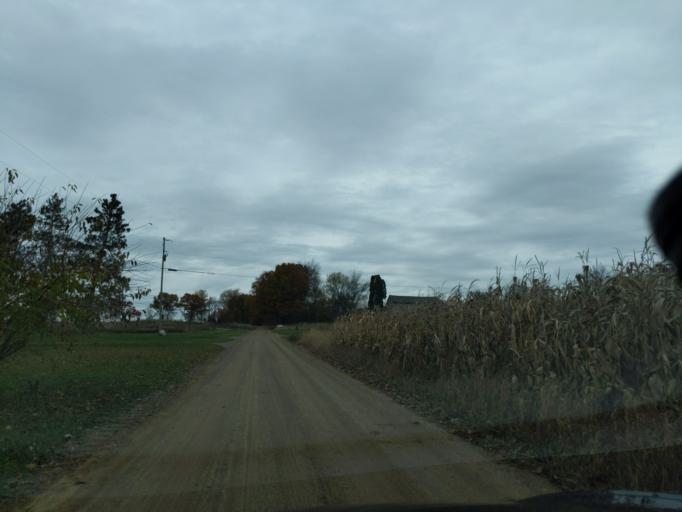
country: US
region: Michigan
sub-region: Eaton County
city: Eaton Rapids
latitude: 42.4278
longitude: -84.6005
